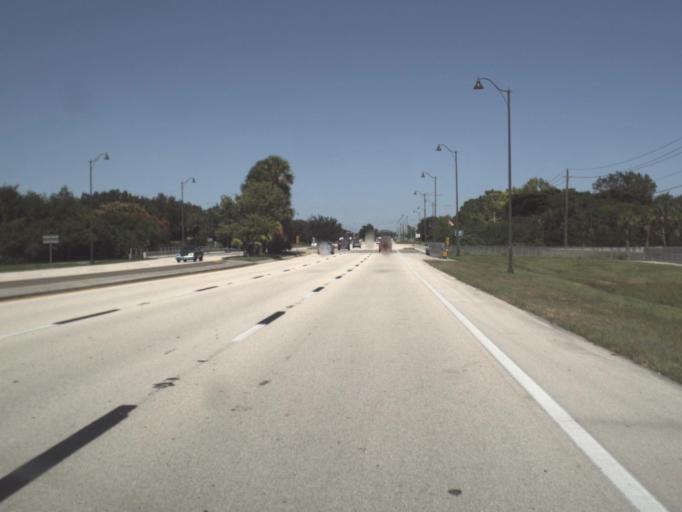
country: US
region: Florida
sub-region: Lee County
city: Bonita Springs
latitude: 26.3637
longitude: -81.8077
